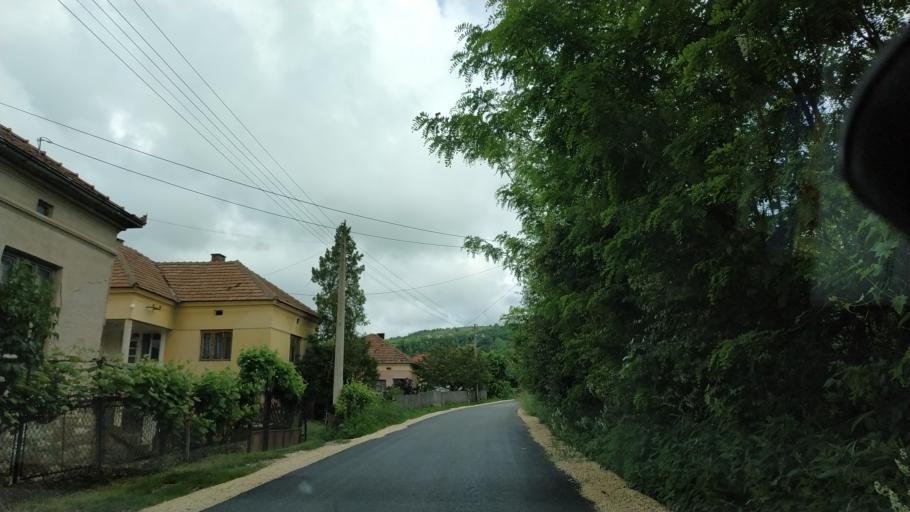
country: RS
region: Central Serbia
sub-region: Zajecarski Okrug
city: Soko Banja
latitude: 43.6768
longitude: 21.9148
